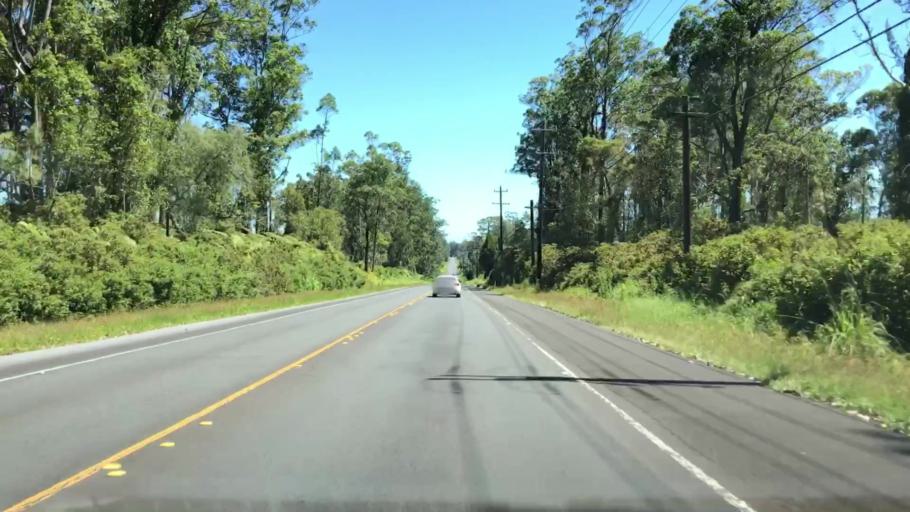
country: US
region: Hawaii
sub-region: Hawaii County
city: Volcano
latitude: 19.4785
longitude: -155.1584
